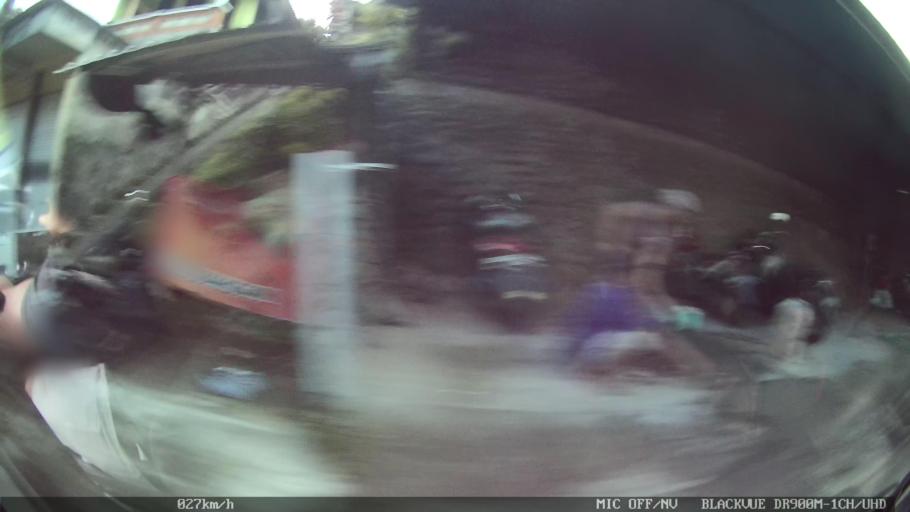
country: ID
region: Bali
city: Banjar Pesalakan
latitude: -8.4919
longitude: 115.2978
